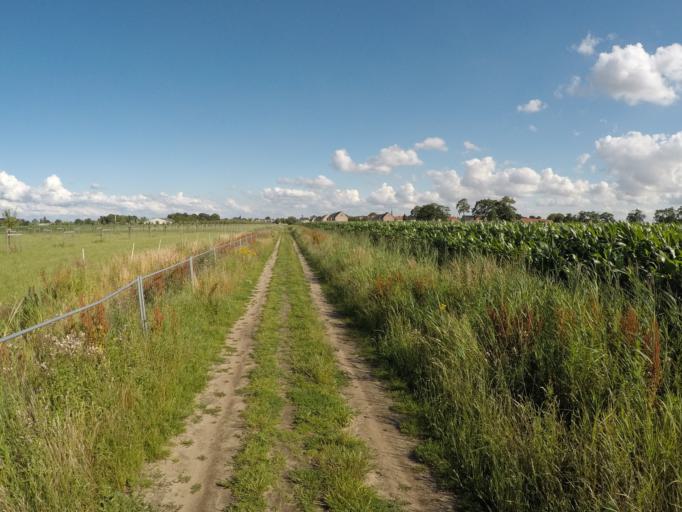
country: BE
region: Flanders
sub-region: Provincie Antwerpen
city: Stabroek
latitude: 51.3398
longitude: 4.3594
